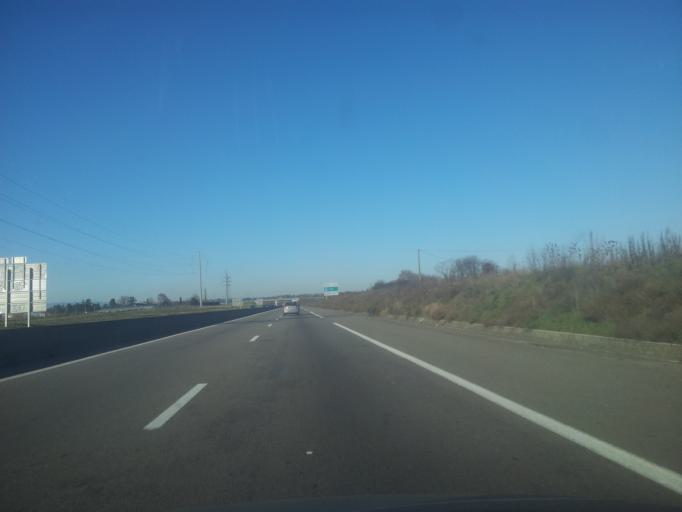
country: FR
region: Rhone-Alpes
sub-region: Departement de la Drome
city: Saint-Marcel-les-Valence
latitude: 44.9411
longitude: 4.9428
